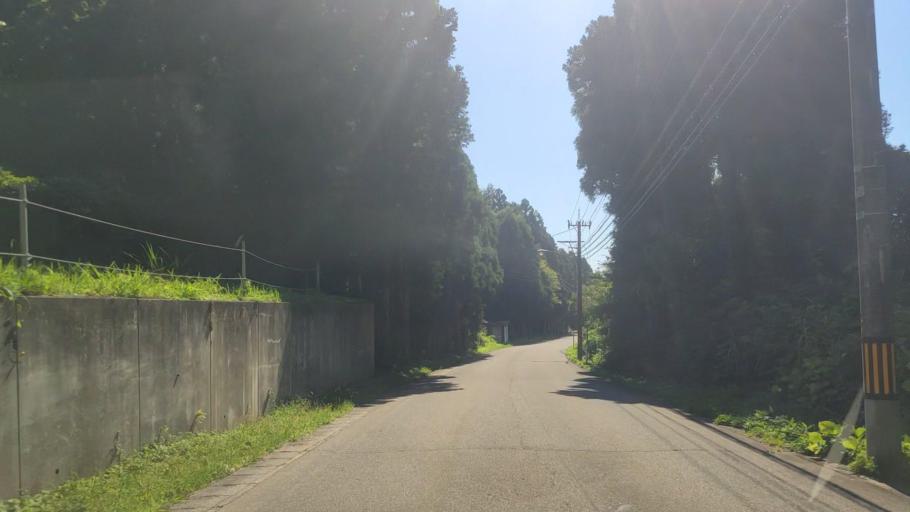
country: JP
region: Ishikawa
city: Nanao
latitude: 37.4542
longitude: 137.3014
